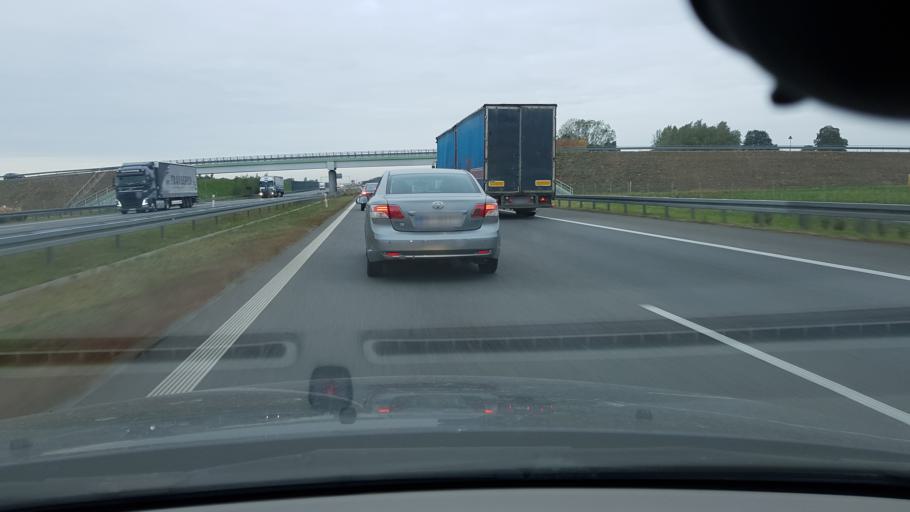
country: PL
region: Masovian Voivodeship
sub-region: Powiat grodziski
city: Grodzisk Mazowiecki
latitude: 52.1433
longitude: 20.5993
